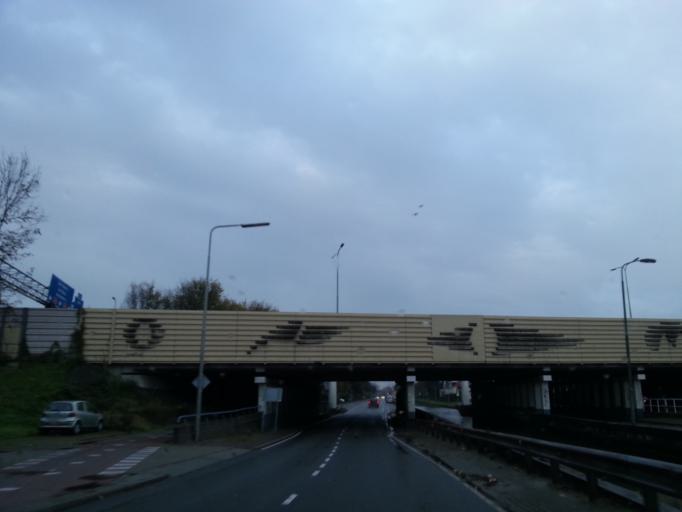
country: NL
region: South Holland
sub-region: Gemeente Delft
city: Delft
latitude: 52.0064
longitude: 4.3825
